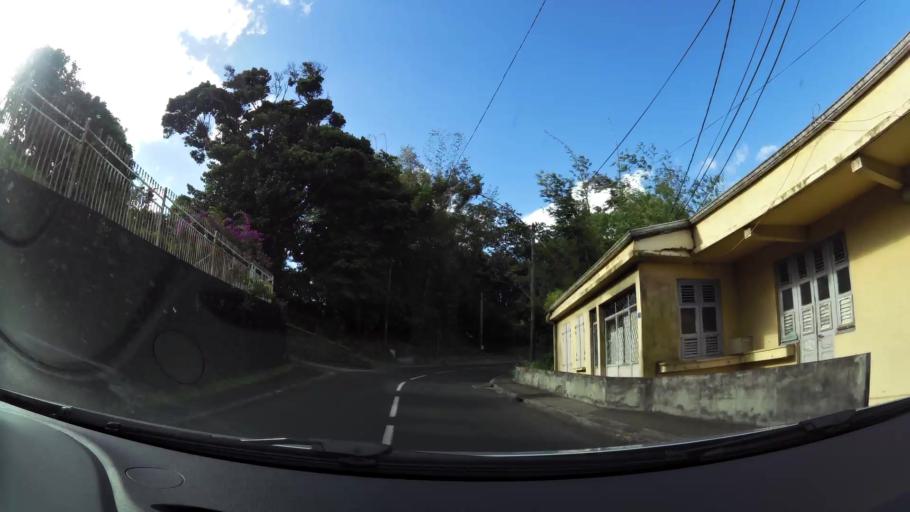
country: MQ
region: Martinique
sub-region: Martinique
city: Fort-de-France
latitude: 14.6511
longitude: -61.0859
